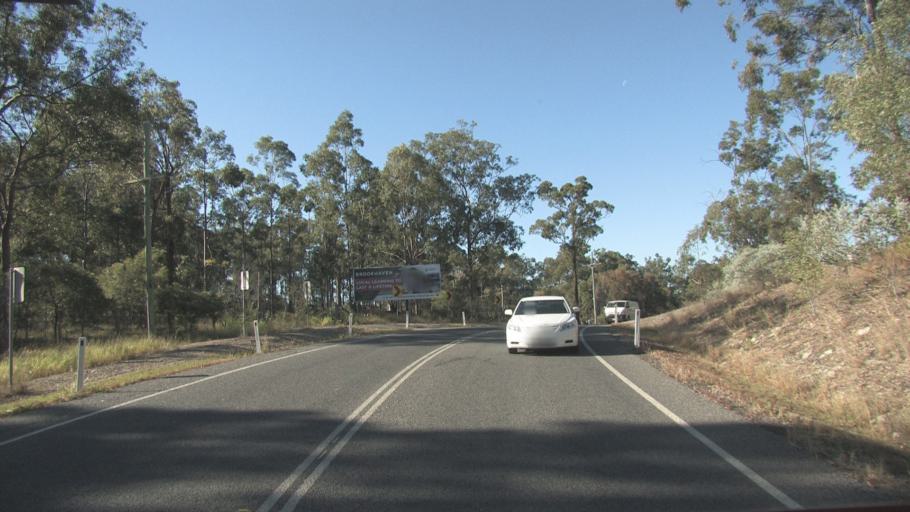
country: AU
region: Queensland
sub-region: Logan
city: Windaroo
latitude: -27.7368
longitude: 153.1545
